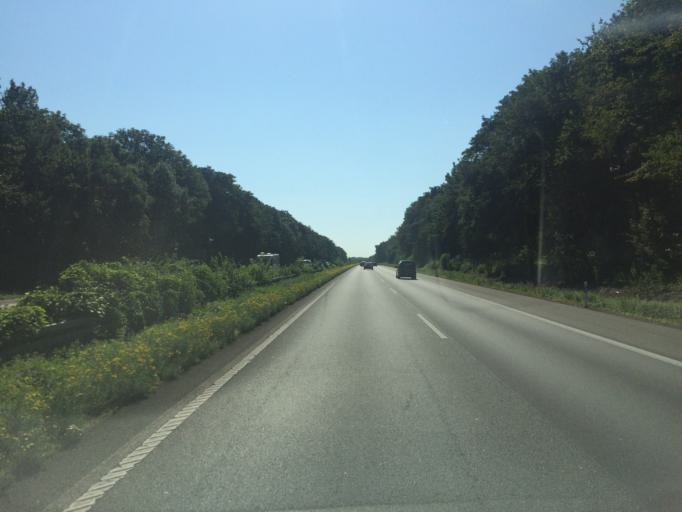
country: DE
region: North Rhine-Westphalia
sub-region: Regierungsbezirk Munster
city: Ascheberg
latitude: 51.7384
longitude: 7.6505
